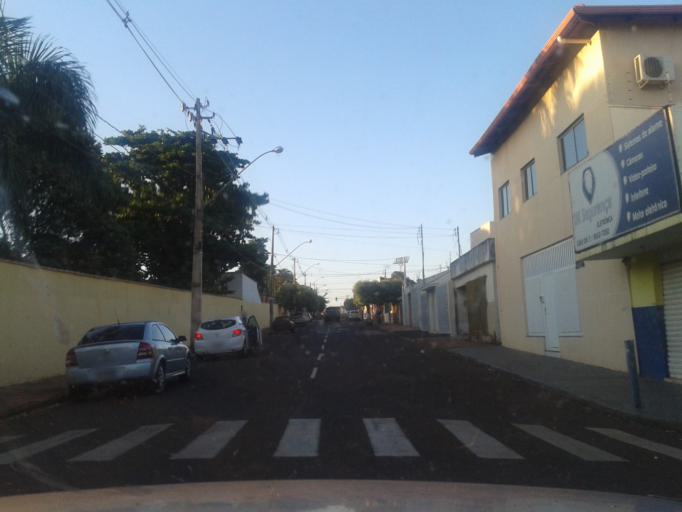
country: BR
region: Minas Gerais
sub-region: Ituiutaba
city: Ituiutaba
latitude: -18.9813
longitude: -49.4646
